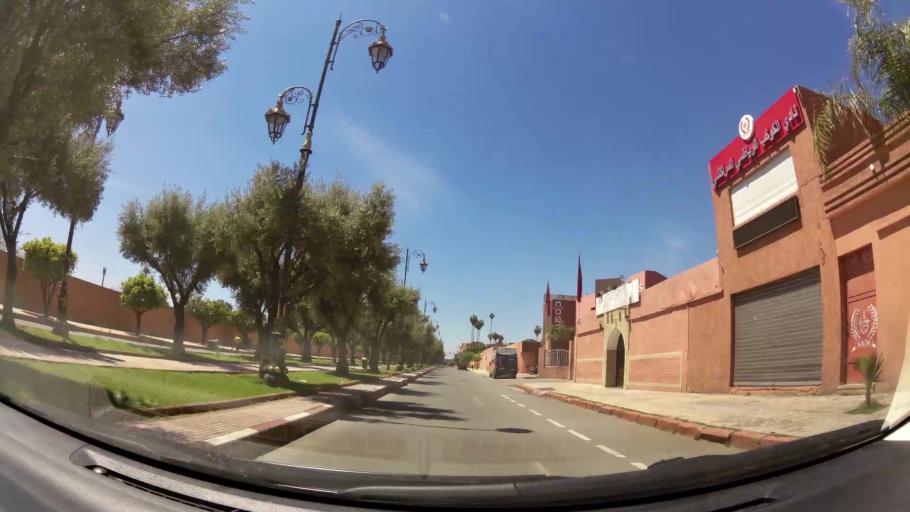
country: MA
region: Marrakech-Tensift-Al Haouz
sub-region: Marrakech
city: Marrakesh
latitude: 31.6268
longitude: -8.0077
